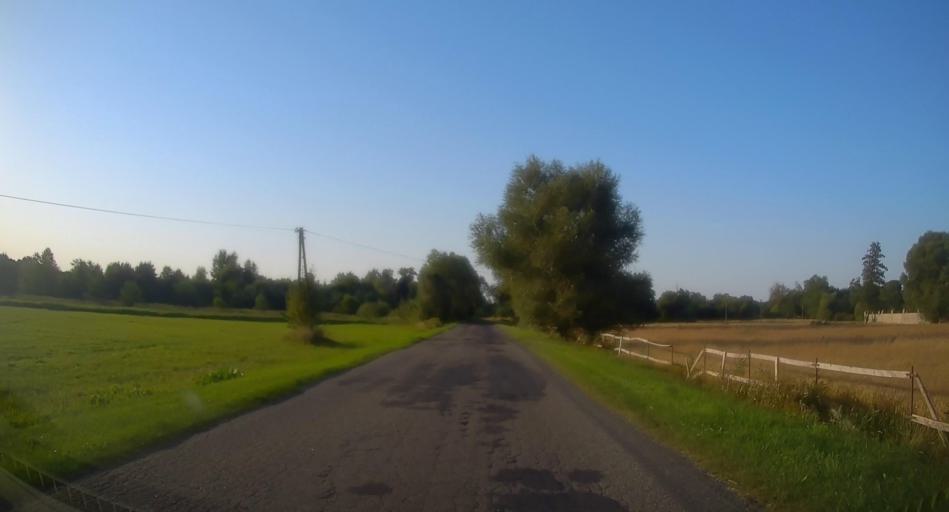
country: PL
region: Lodz Voivodeship
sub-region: Powiat skierniewicki
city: Kaweczyn Nowy
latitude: 51.8982
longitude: 20.2984
